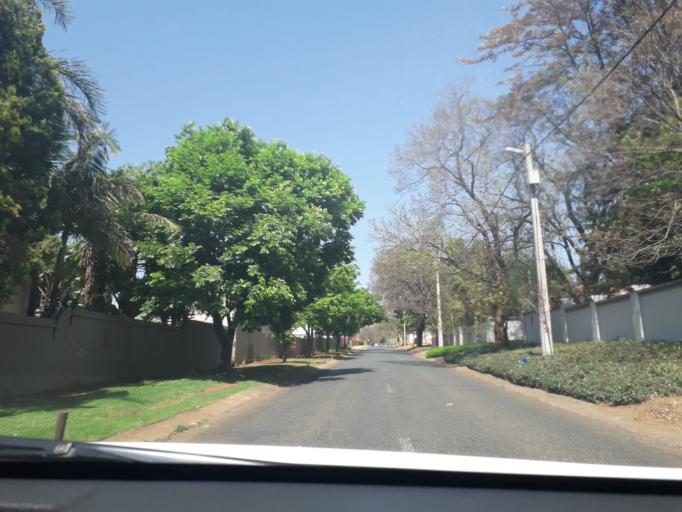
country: ZA
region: Gauteng
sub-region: City of Johannesburg Metropolitan Municipality
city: Roodepoort
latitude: -26.1328
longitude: 27.9495
